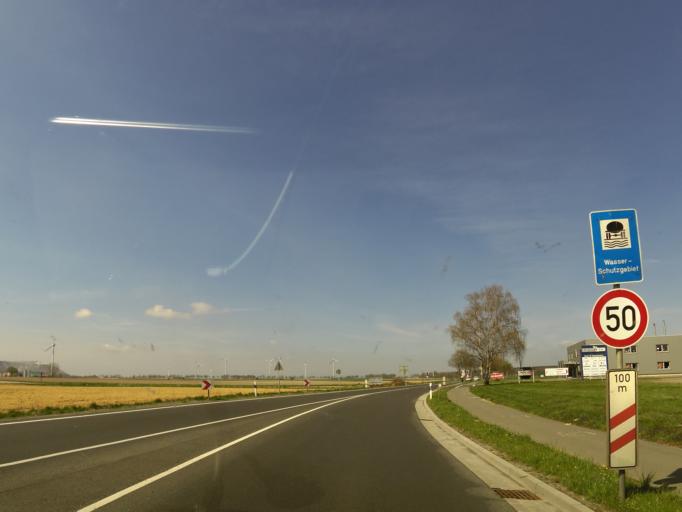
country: DE
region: Lower Saxony
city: Wunstorf
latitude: 52.4267
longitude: 9.4041
